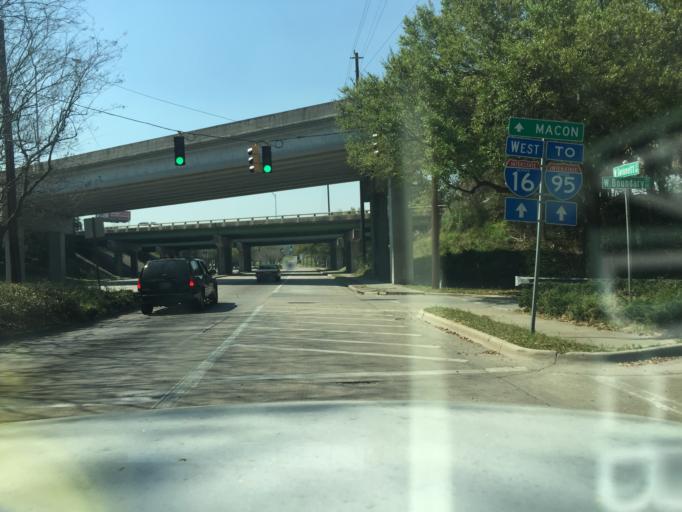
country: US
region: Georgia
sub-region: Chatham County
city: Savannah
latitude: 32.0698
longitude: -81.1061
